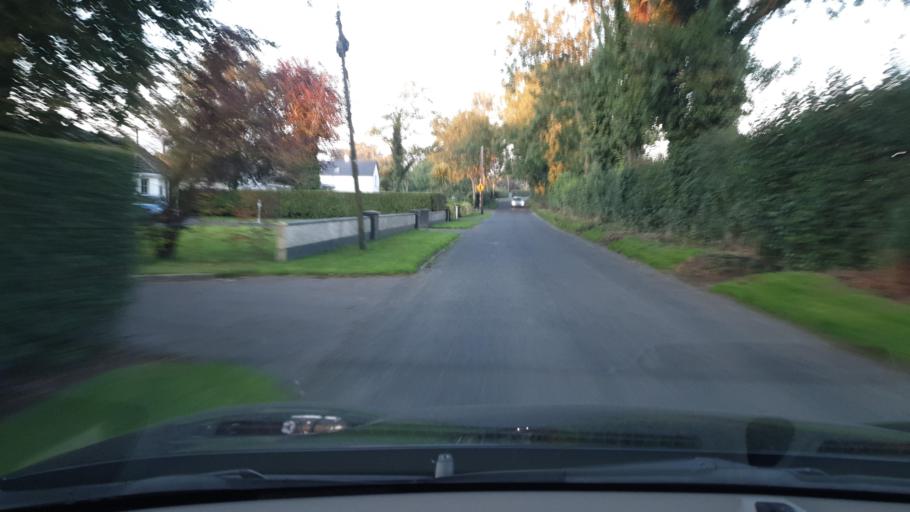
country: IE
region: Leinster
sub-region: Kildare
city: Prosperous
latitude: 53.3177
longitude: -6.8155
